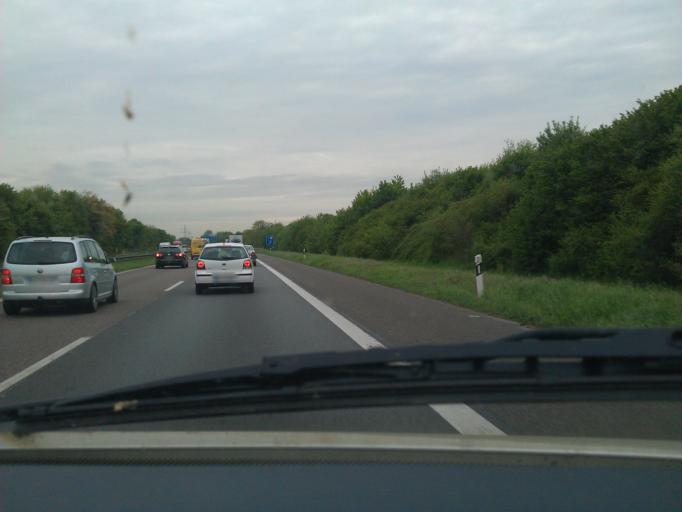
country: DE
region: North Rhine-Westphalia
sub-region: Regierungsbezirk Dusseldorf
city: Moers
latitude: 51.4698
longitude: 6.5888
